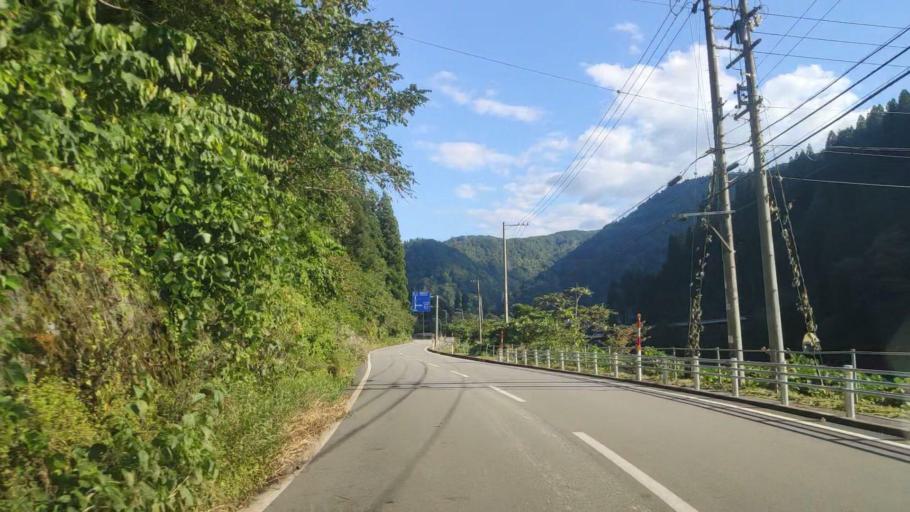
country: JP
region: Gifu
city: Takayama
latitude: 36.3055
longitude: 137.1106
